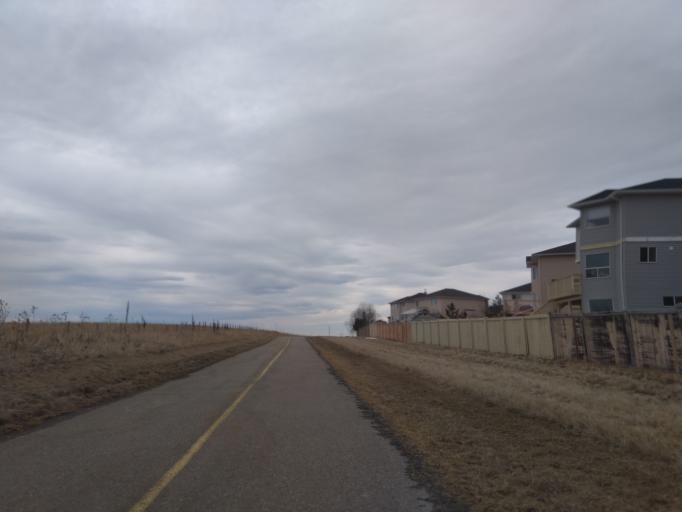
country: CA
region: Alberta
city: Chestermere
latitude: 51.1025
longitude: -113.9228
